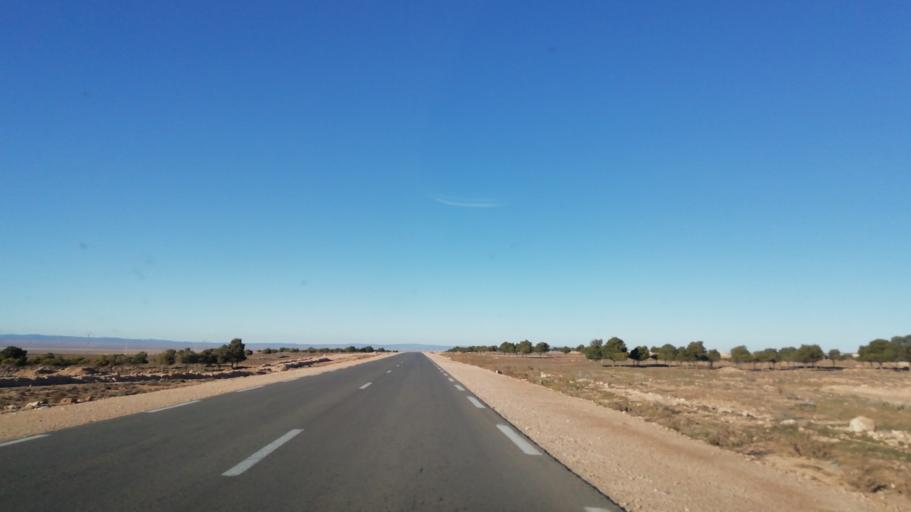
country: DZ
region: Tlemcen
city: Sebdou
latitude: 34.2817
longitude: -1.2593
